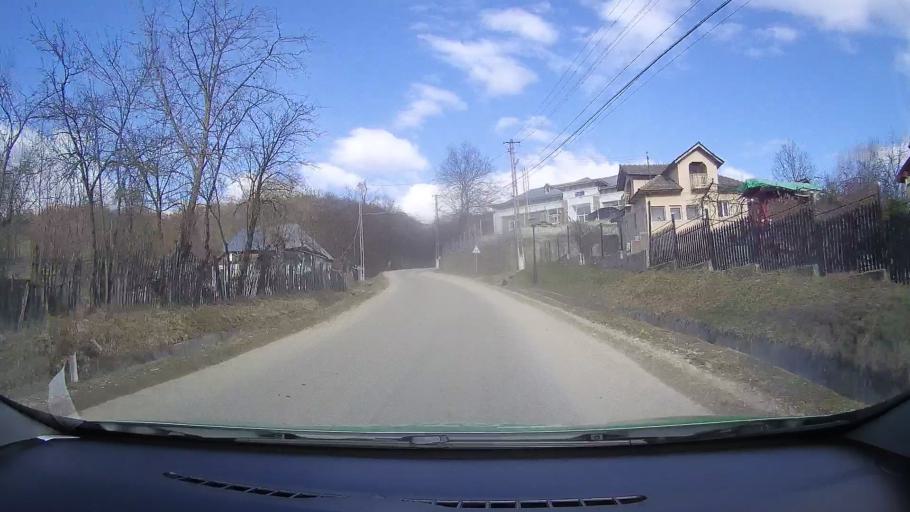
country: RO
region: Dambovita
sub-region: Comuna Varfuri
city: Varfuri
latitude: 45.0933
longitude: 25.5080
